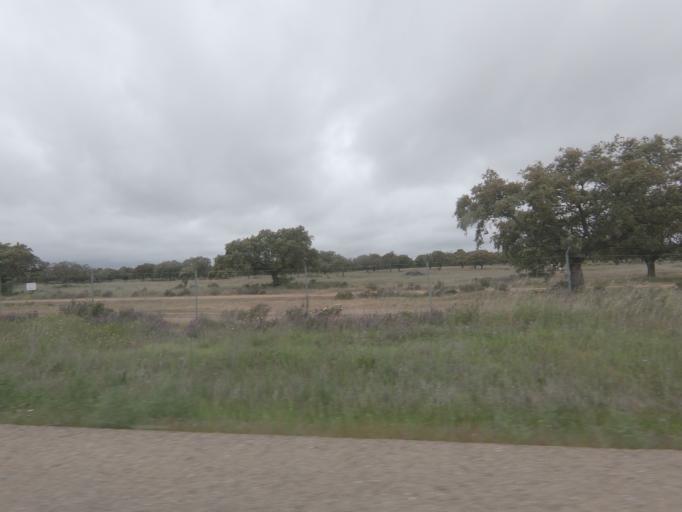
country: ES
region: Extremadura
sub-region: Provincia de Badajoz
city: Villar del Rey
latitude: 38.9991
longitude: -6.8671
